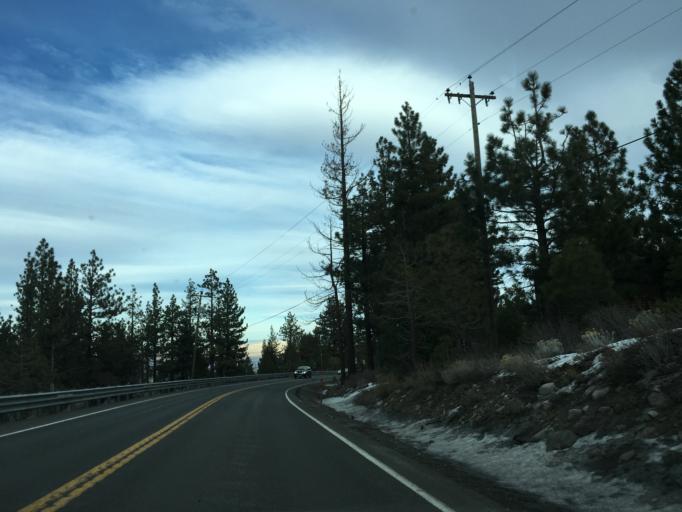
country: US
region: Nevada
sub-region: Washoe County
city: Incline Village
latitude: 39.3434
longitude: -119.8643
